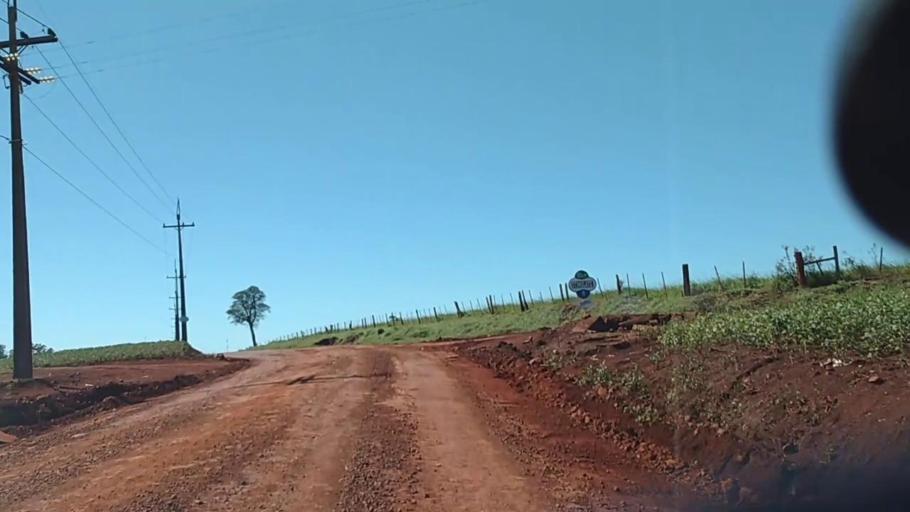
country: PY
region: Alto Parana
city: Naranjal
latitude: -25.9756
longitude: -55.2203
